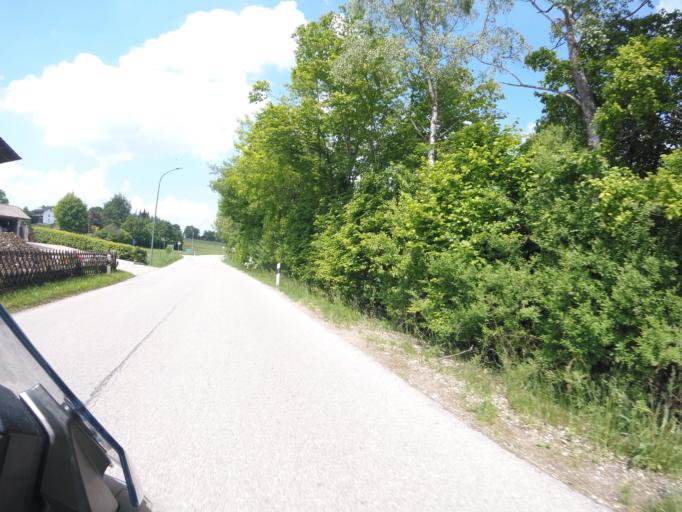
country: DE
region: Bavaria
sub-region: Upper Bavaria
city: Berg
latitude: 47.8825
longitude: 11.3785
